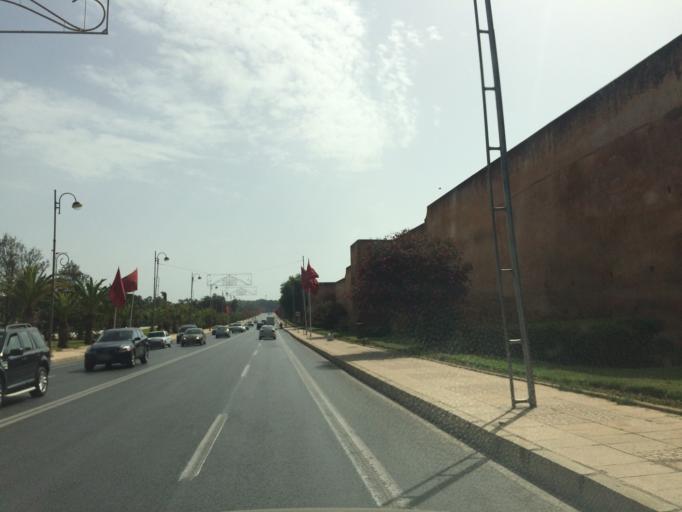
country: MA
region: Rabat-Sale-Zemmour-Zaer
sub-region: Rabat
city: Rabat
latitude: 34.0049
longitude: -6.8282
